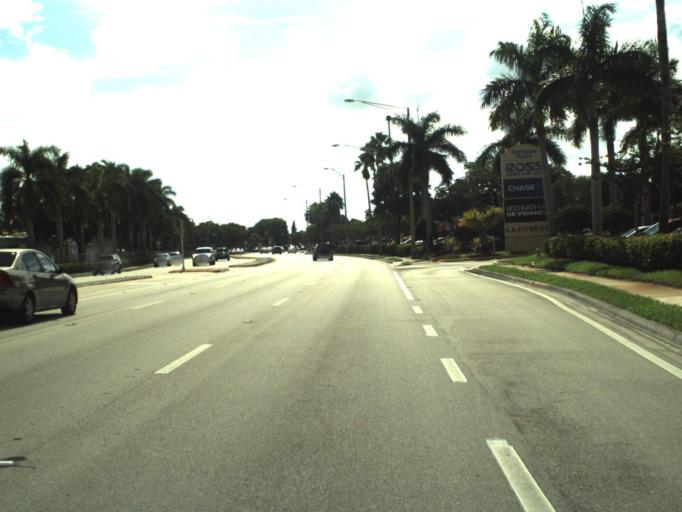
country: US
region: Florida
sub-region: Broward County
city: Pembroke Pines
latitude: 26.0327
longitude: -80.1976
